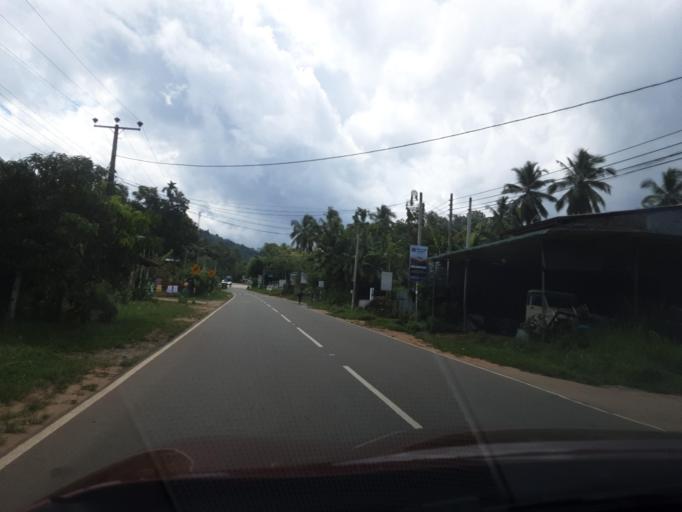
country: LK
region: Uva
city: Monaragala
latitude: 6.8979
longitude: 81.2424
